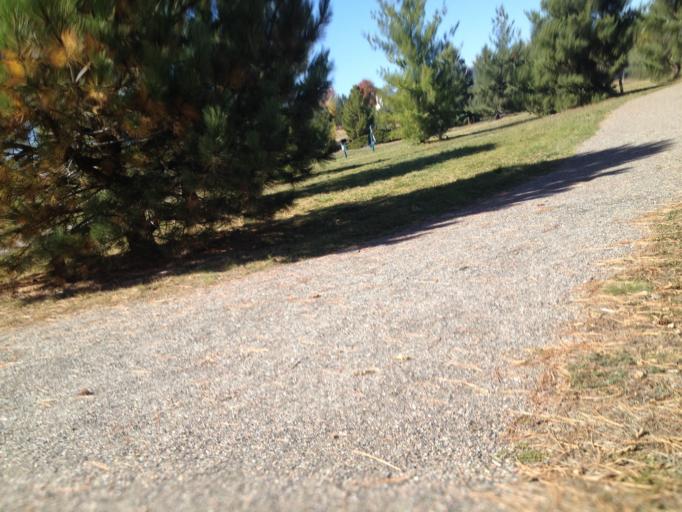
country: US
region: Colorado
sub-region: Boulder County
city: Superior
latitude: 39.9725
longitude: -105.1604
